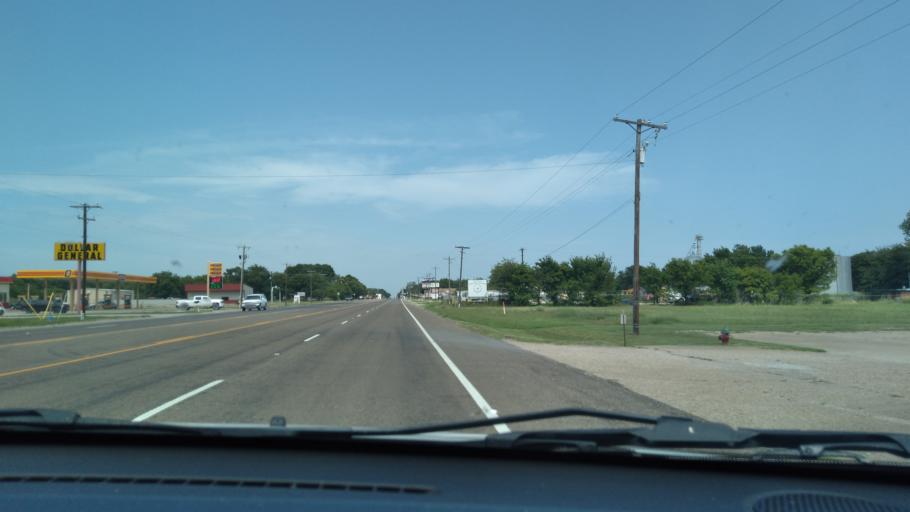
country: US
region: Texas
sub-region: Navarro County
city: Kerens
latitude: 32.1312
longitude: -96.2412
